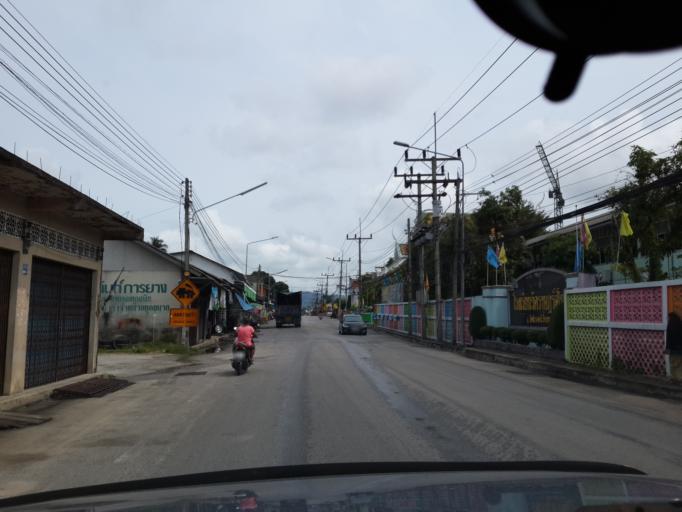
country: TH
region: Narathiwat
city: Rueso
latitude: 6.3871
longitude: 101.5137
